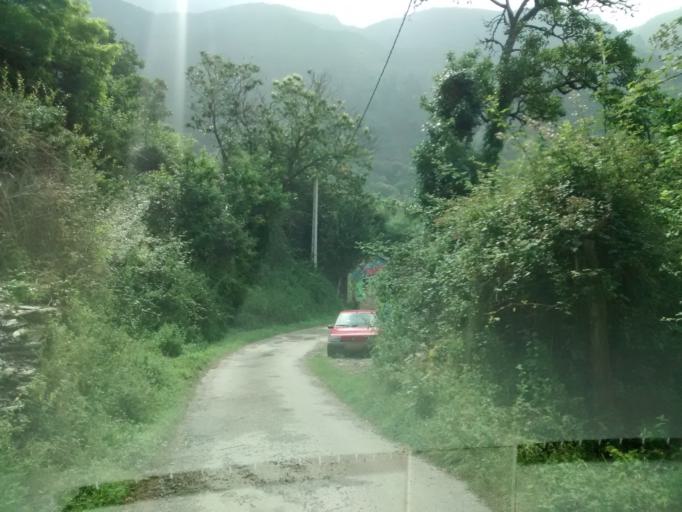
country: ES
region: Galicia
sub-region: Provincia de Ourense
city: Castro Caldelas
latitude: 42.4246
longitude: -7.3901
